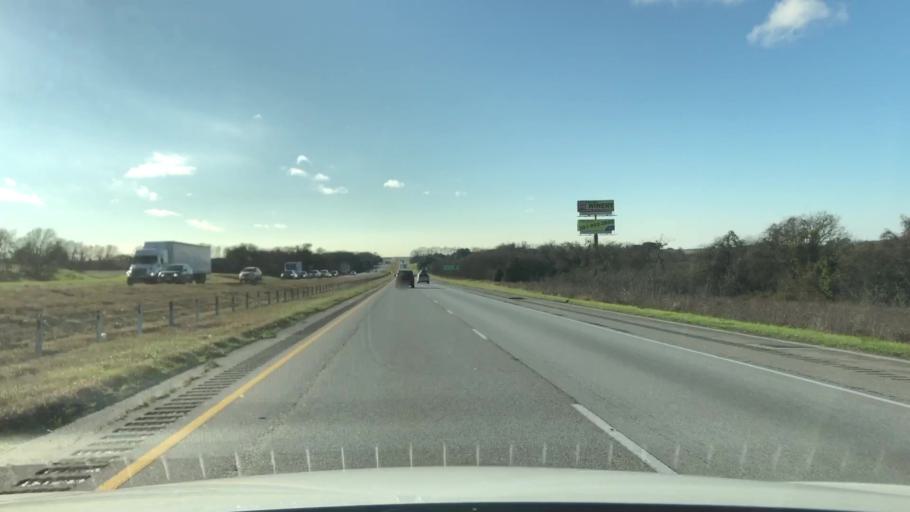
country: US
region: Texas
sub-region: Colorado County
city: Weimar
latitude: 29.6910
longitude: -96.7879
